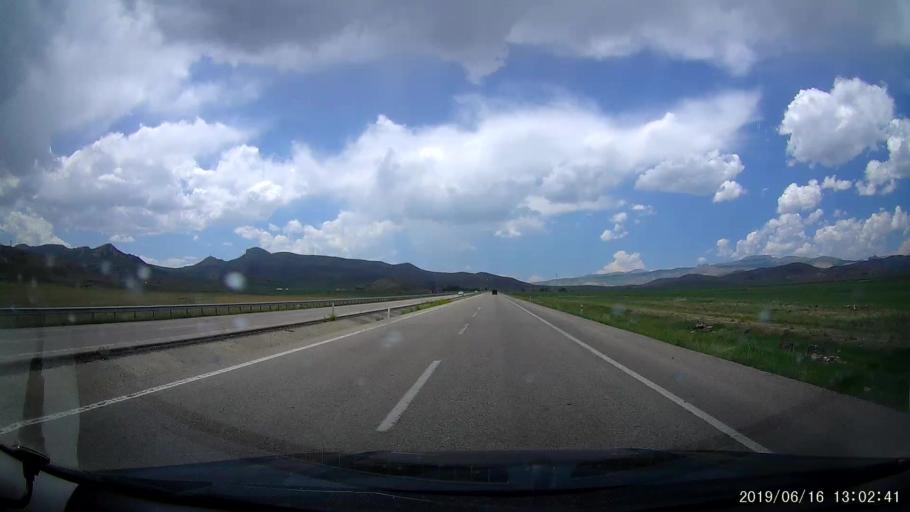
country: TR
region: Agri
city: Sulucem
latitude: 39.5761
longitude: 43.8096
